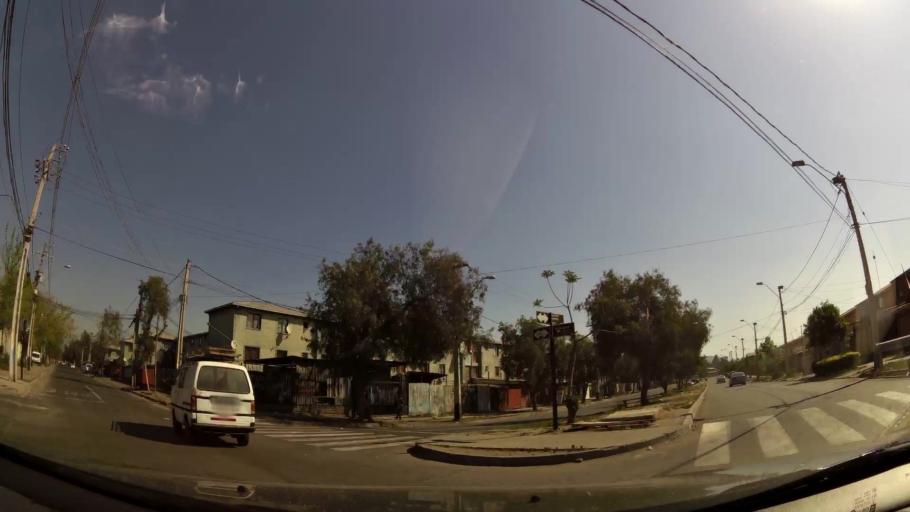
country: CL
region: Santiago Metropolitan
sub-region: Provincia de Santiago
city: La Pintana
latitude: -33.6234
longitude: -70.6237
